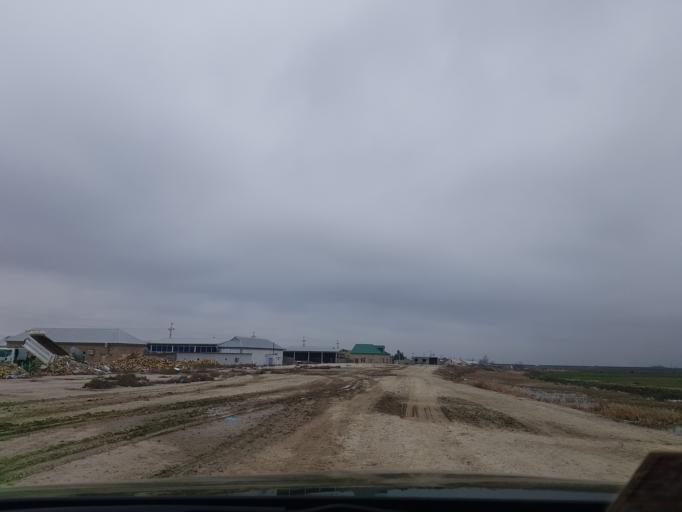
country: TM
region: Ahal
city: Abadan
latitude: 38.1437
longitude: 57.9640
